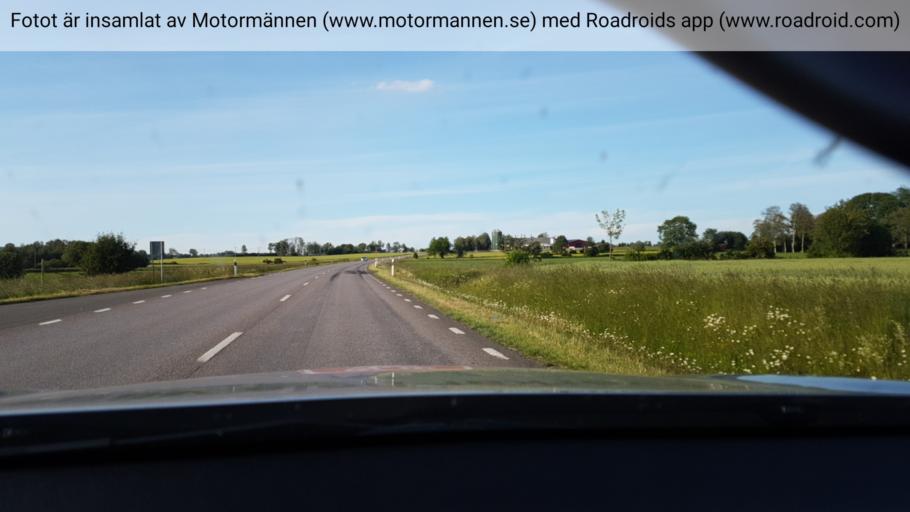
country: SE
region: Vaestra Goetaland
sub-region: Falkopings Kommun
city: Falkoeping
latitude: 58.1192
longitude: 13.5456
